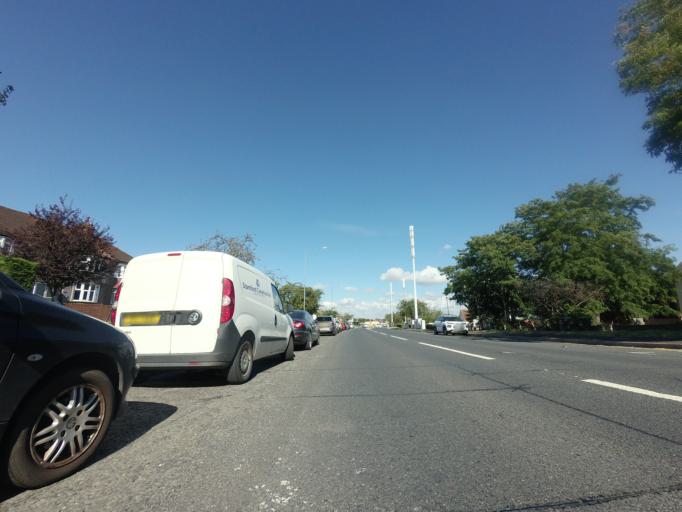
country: GB
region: England
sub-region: Kent
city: Gravesend
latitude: 51.4308
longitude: 0.3975
